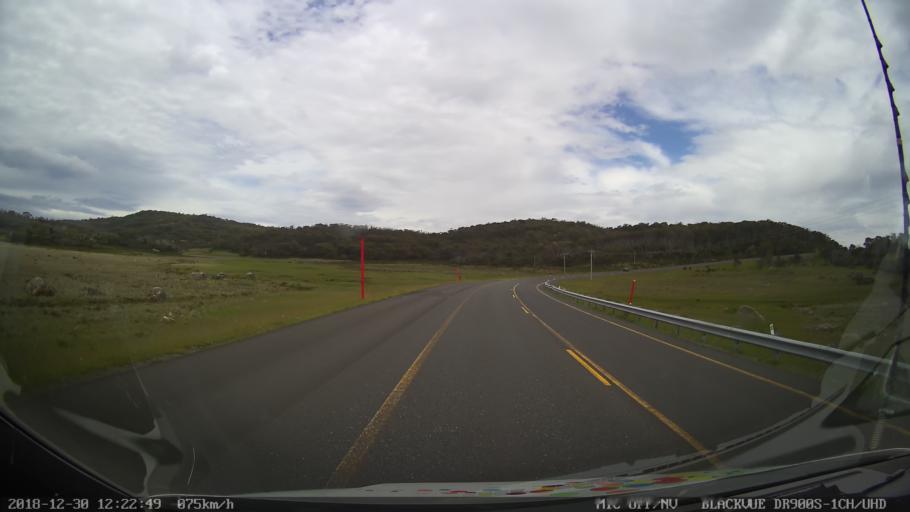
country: AU
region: New South Wales
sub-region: Snowy River
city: Jindabyne
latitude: -36.3612
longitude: 148.5071
